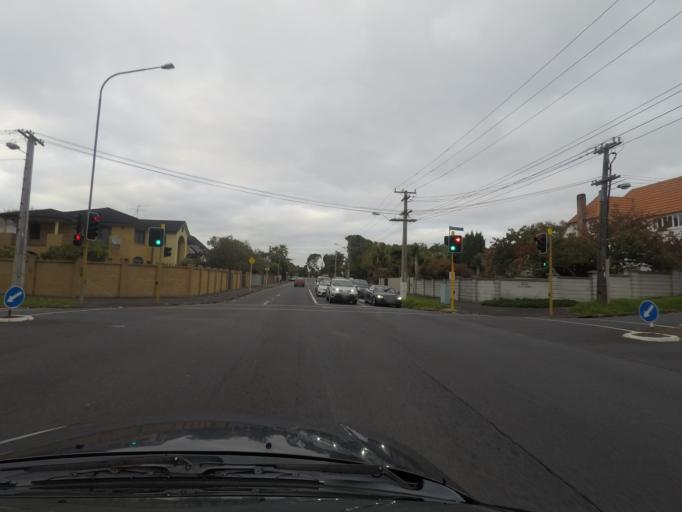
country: NZ
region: Auckland
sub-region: Auckland
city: Auckland
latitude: -36.8828
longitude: 174.7716
